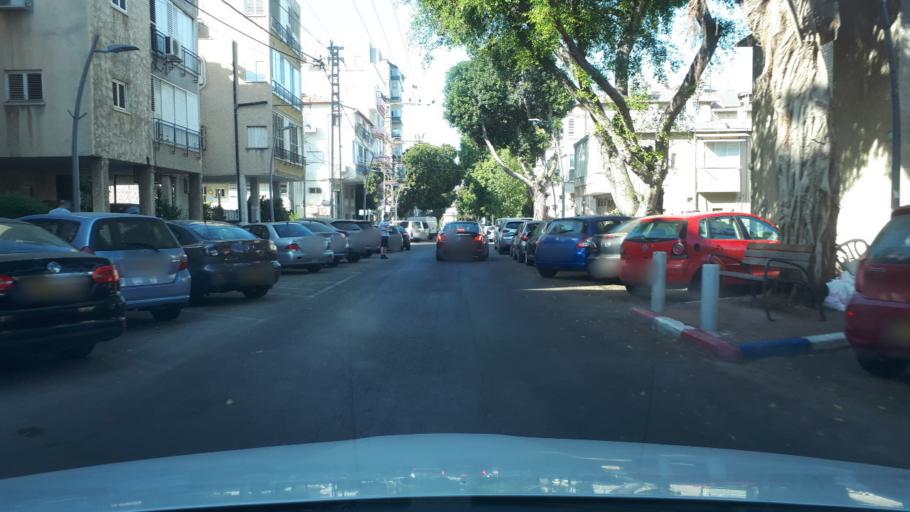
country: IL
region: Tel Aviv
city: Bene Beraq
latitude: 32.0773
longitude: 34.8232
